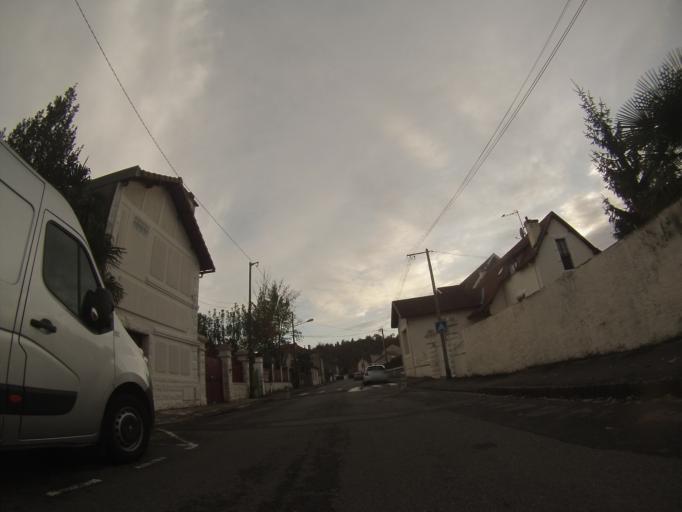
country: FR
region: Aquitaine
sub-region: Departement des Pyrenees-Atlantiques
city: Jurancon
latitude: 43.2858
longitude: -0.3807
